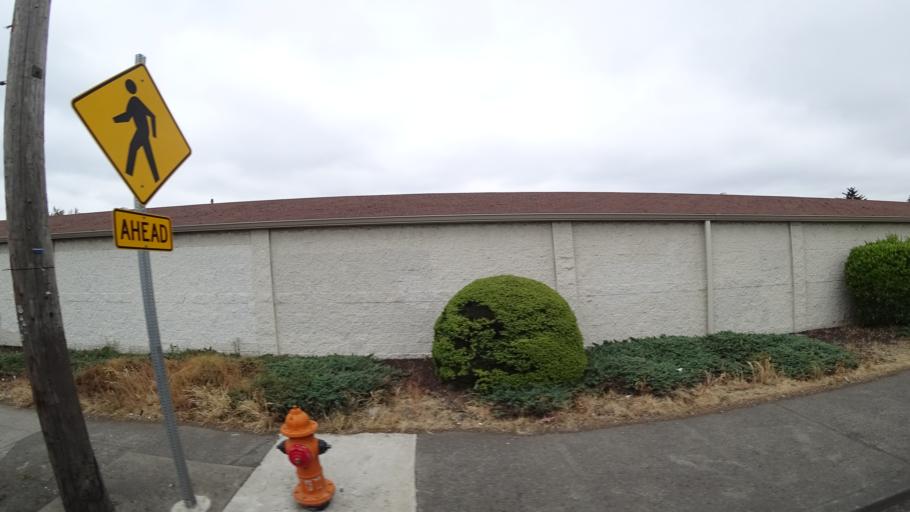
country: US
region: Oregon
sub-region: Multnomah County
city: Lents
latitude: 45.5135
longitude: -122.5787
